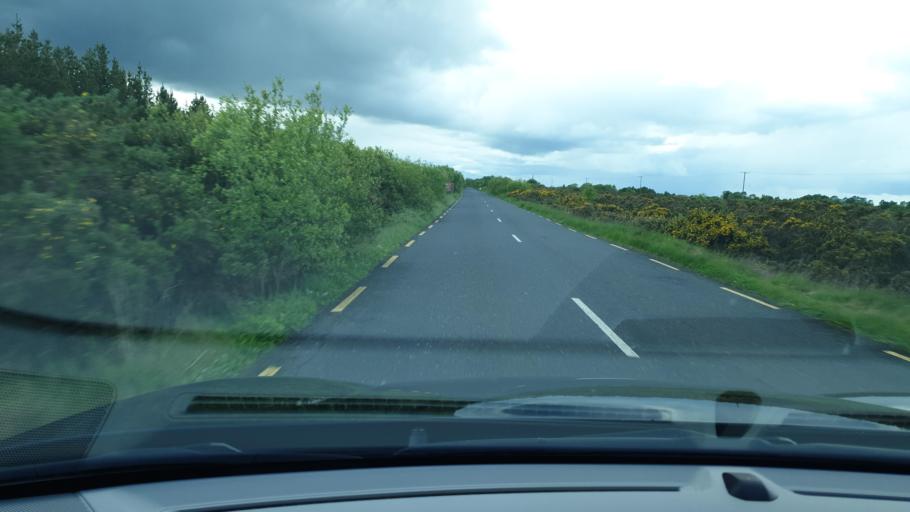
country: IE
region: Leinster
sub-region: Uibh Fhaili
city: Clara
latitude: 53.2380
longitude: -7.6938
